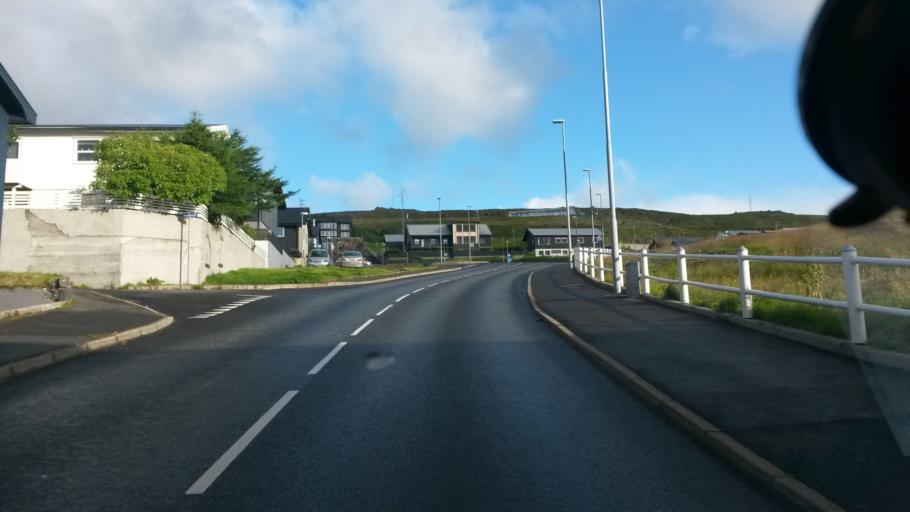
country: FO
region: Streymoy
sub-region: Torshavn
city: Torshavn
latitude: 62.0113
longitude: -6.7903
